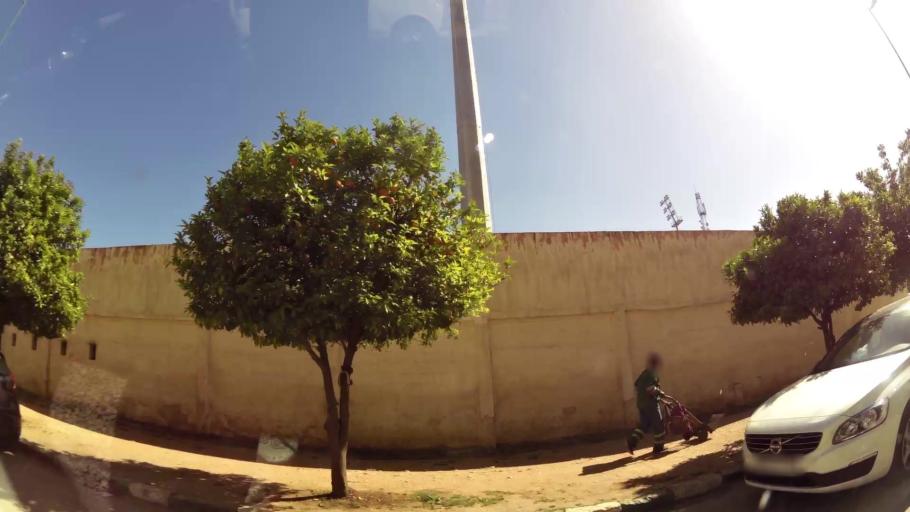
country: MA
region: Meknes-Tafilalet
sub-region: Meknes
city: Meknes
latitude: 33.8924
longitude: -5.5394
